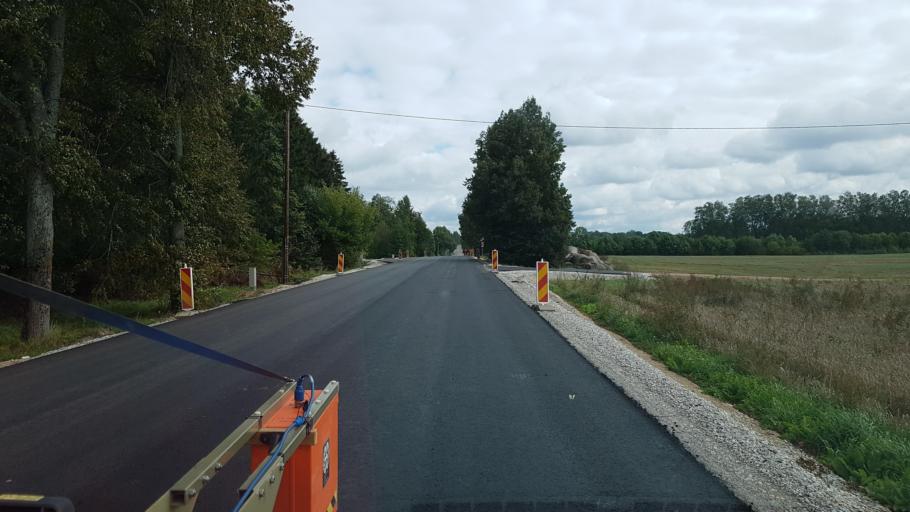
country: EE
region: Tartu
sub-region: Elva linn
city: Elva
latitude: 58.0086
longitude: 26.2256
